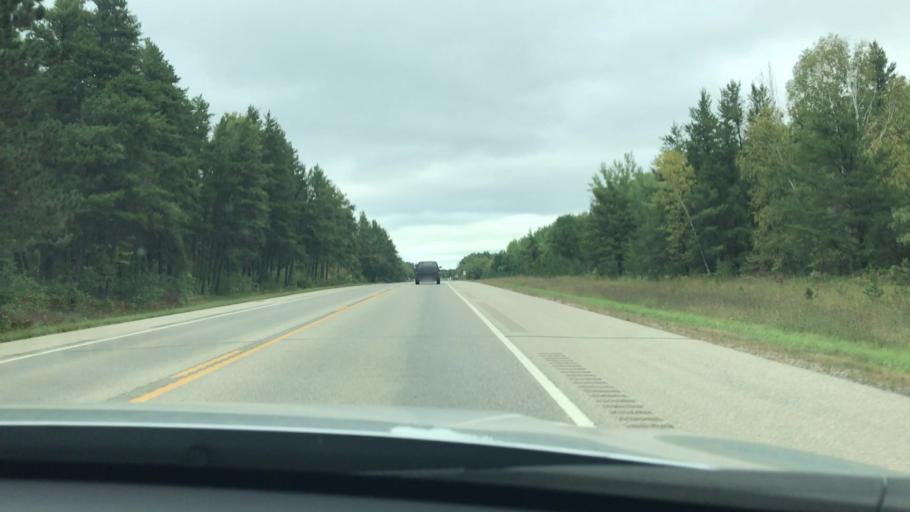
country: US
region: Minnesota
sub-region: Wadena County
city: Menahga
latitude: 46.8295
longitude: -95.0890
